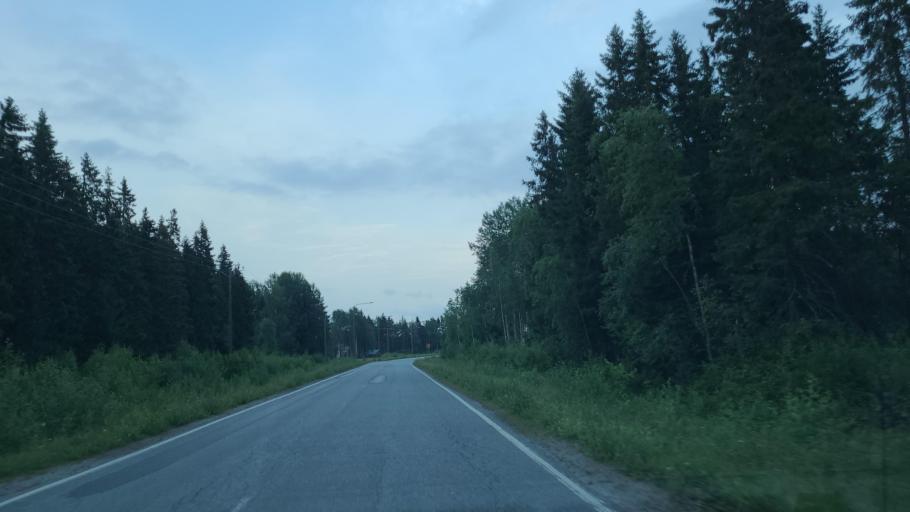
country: FI
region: Ostrobothnia
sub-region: Vaasa
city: Replot
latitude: 63.2017
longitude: 21.2963
